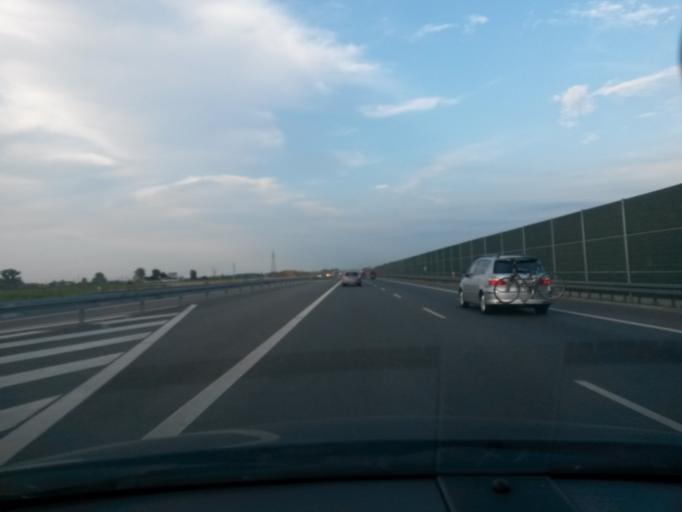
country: PL
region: Masovian Voivodeship
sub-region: Powiat warszawski zachodni
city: Bieniewice
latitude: 52.1324
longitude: 20.5537
